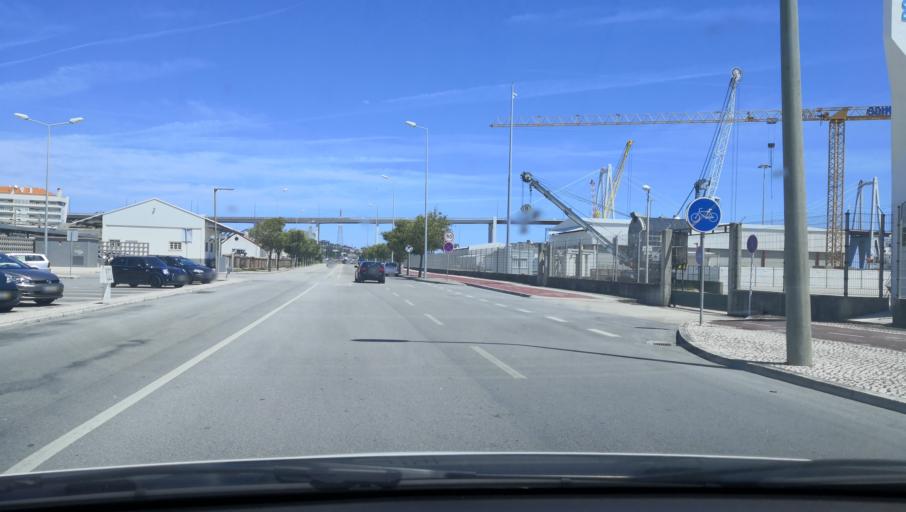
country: PT
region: Coimbra
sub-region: Figueira da Foz
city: Figueira da Foz
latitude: 40.1480
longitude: -8.8485
